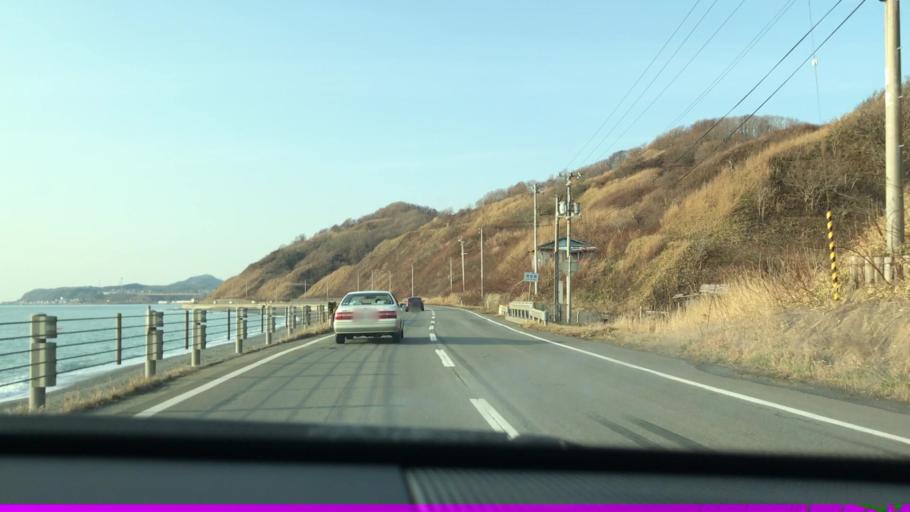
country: JP
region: Hokkaido
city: Shizunai-furukawacho
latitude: 42.2341
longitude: 142.6014
